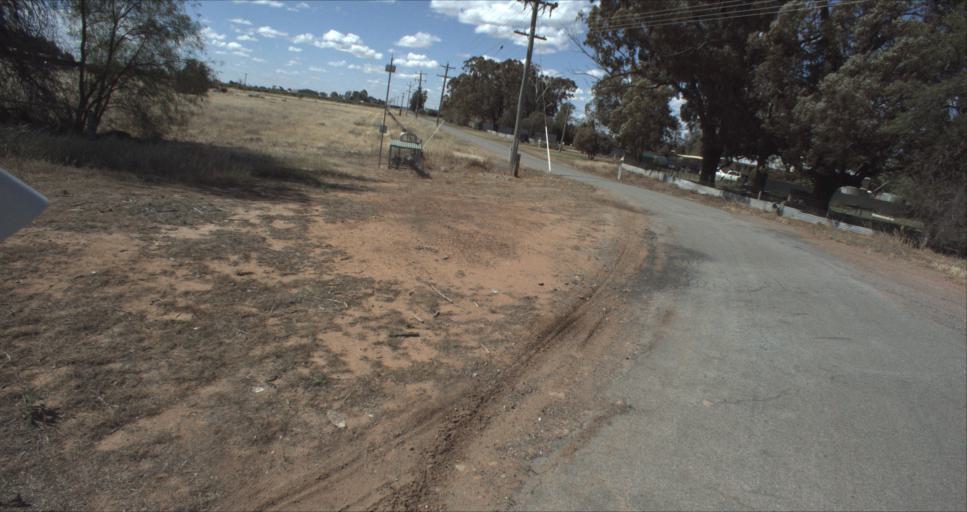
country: AU
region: New South Wales
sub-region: Leeton
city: Leeton
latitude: -34.5153
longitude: 146.2505
